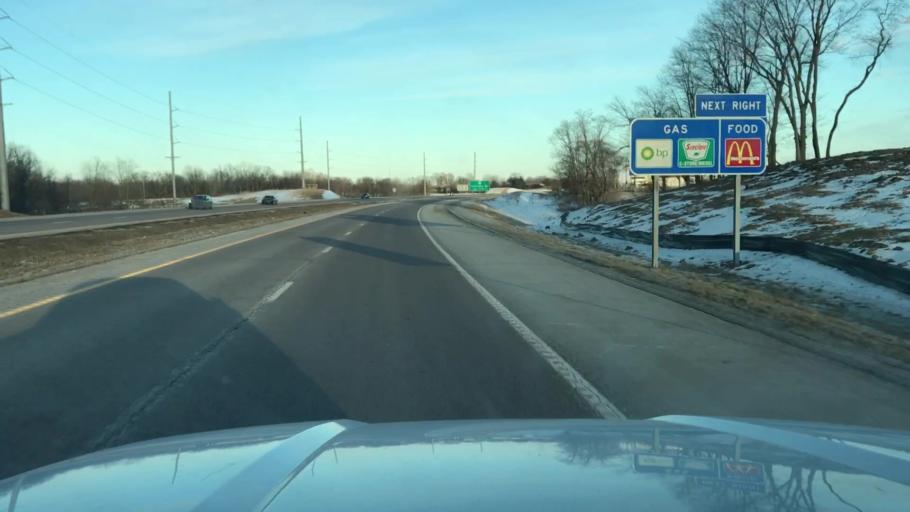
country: US
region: Missouri
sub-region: Buchanan County
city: Saint Joseph
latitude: 39.7511
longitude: -94.7829
